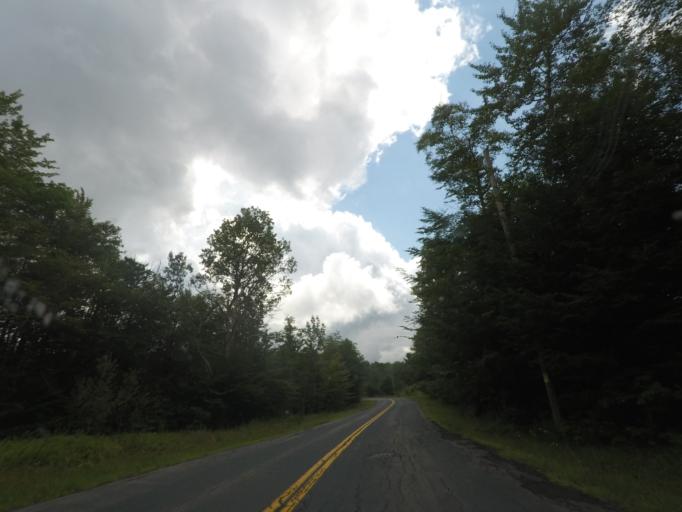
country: US
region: New York
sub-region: Rensselaer County
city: Averill Park
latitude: 42.6616
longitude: -73.4136
